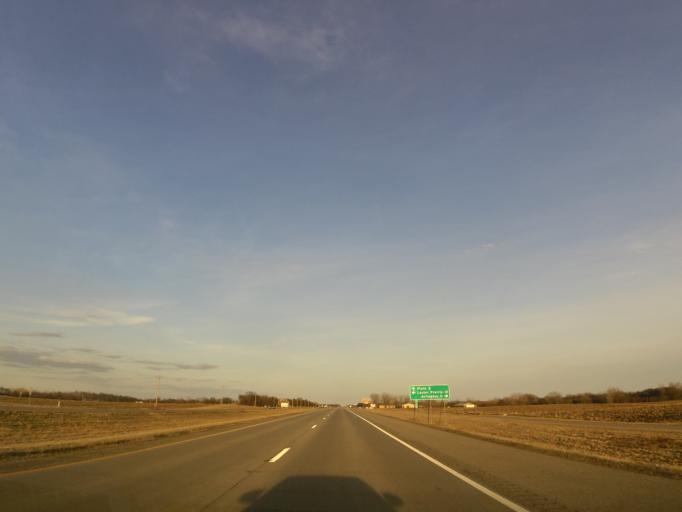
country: US
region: Minnesota
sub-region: McLeod County
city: Glencoe
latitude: 44.7680
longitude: -94.0983
